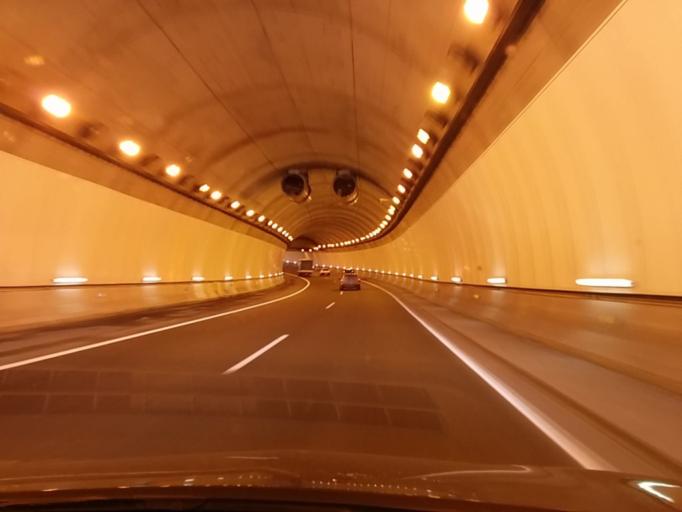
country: ES
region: Basque Country
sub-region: Provincia de Guipuzcoa
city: Errenteria
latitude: 43.3170
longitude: -1.9133
